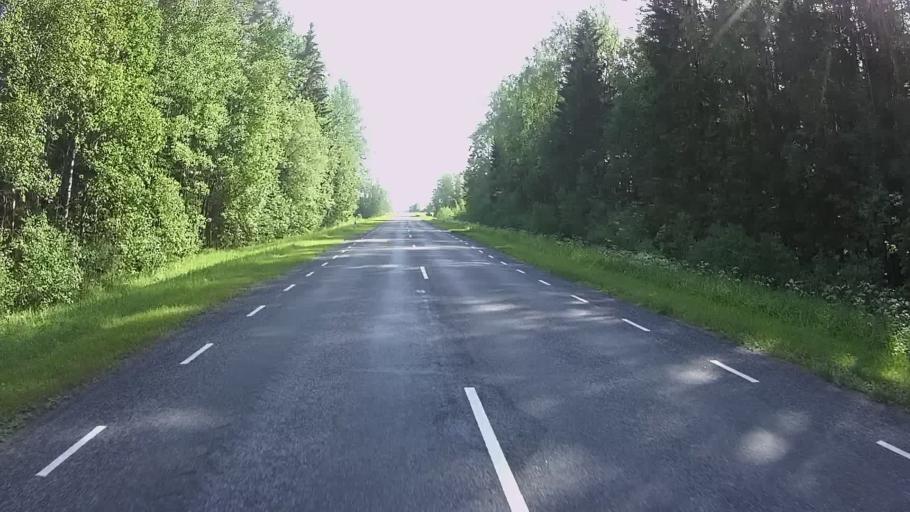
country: EE
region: Valgamaa
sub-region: Torva linn
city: Torva
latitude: 58.0616
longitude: 26.0200
